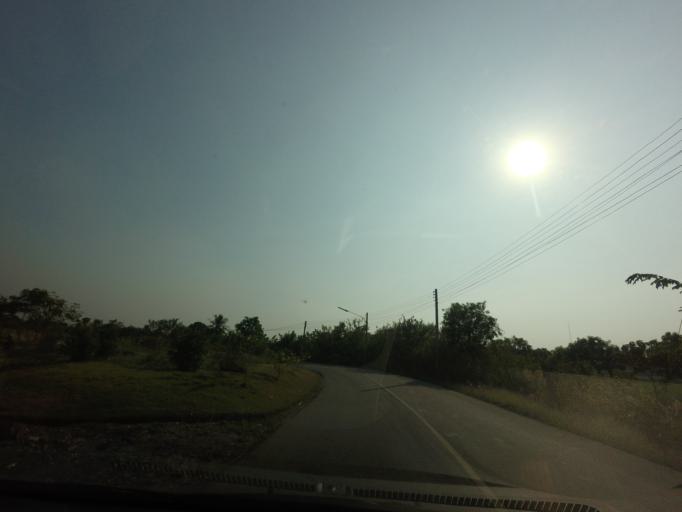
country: TH
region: Chachoengsao
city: Khlong Khuean
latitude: 13.7686
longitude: 101.1741
